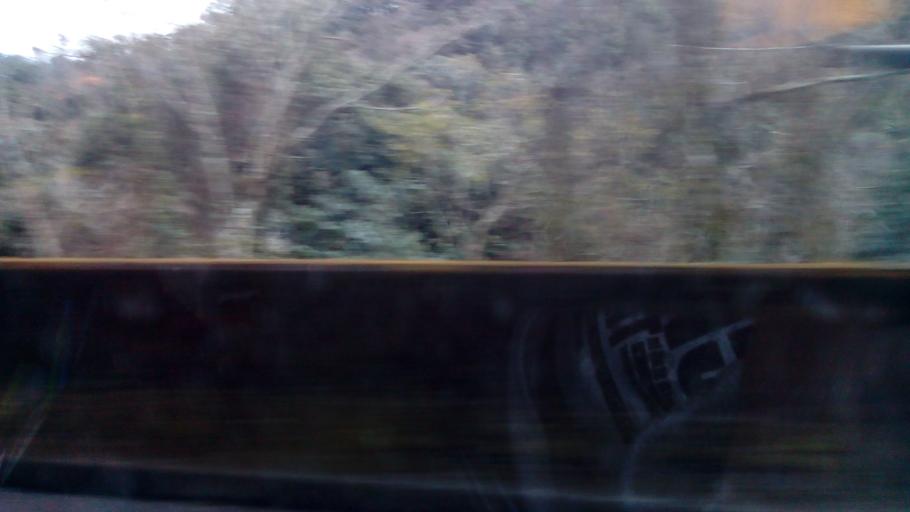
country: TW
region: Taiwan
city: Daxi
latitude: 24.4042
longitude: 121.3652
